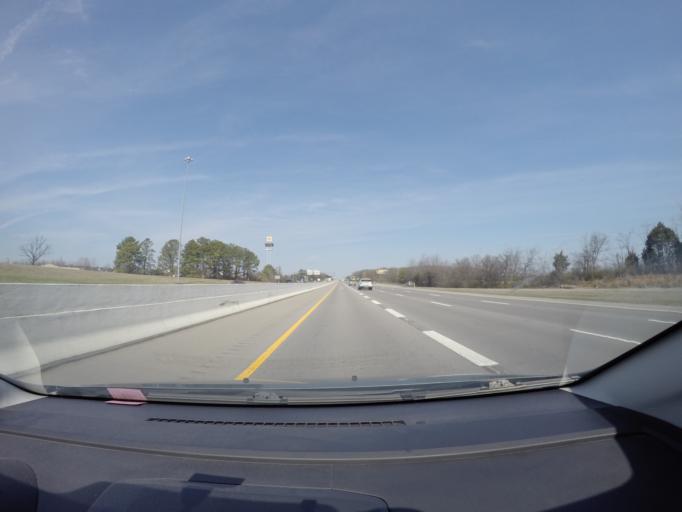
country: US
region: Tennessee
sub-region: Rutherford County
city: Murfreesboro
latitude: 35.8496
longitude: -86.4377
